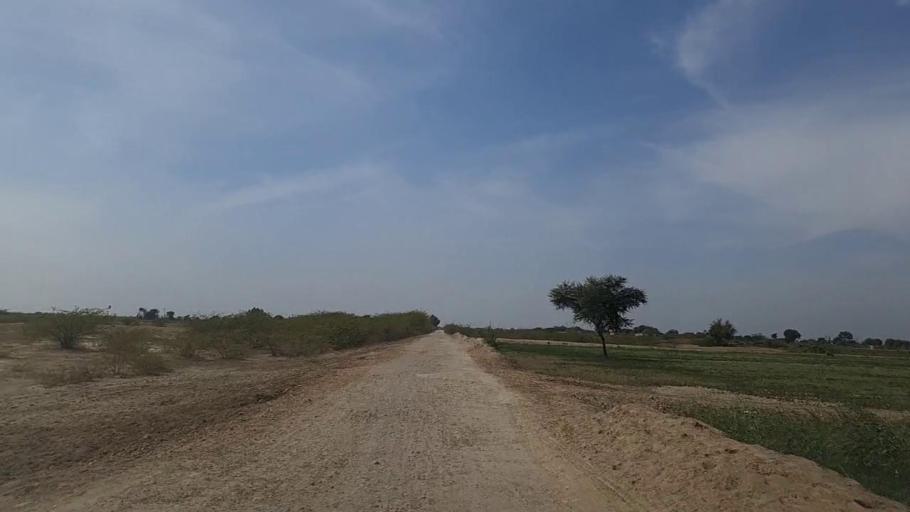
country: PK
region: Sindh
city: Kunri
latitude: 25.2128
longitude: 69.4902
